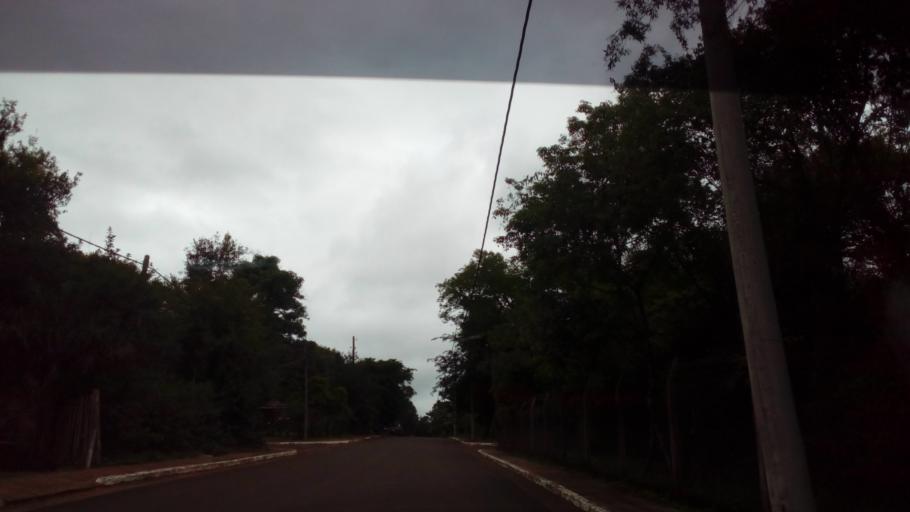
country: AR
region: Misiones
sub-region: Departamento de Candelaria
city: Candelaria
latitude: -27.4497
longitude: -55.7488
